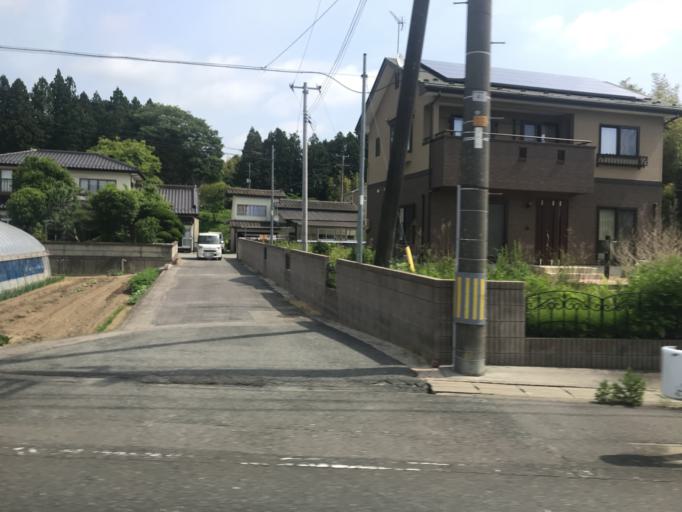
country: JP
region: Fukushima
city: Namie
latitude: 37.3435
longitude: 141.0026
